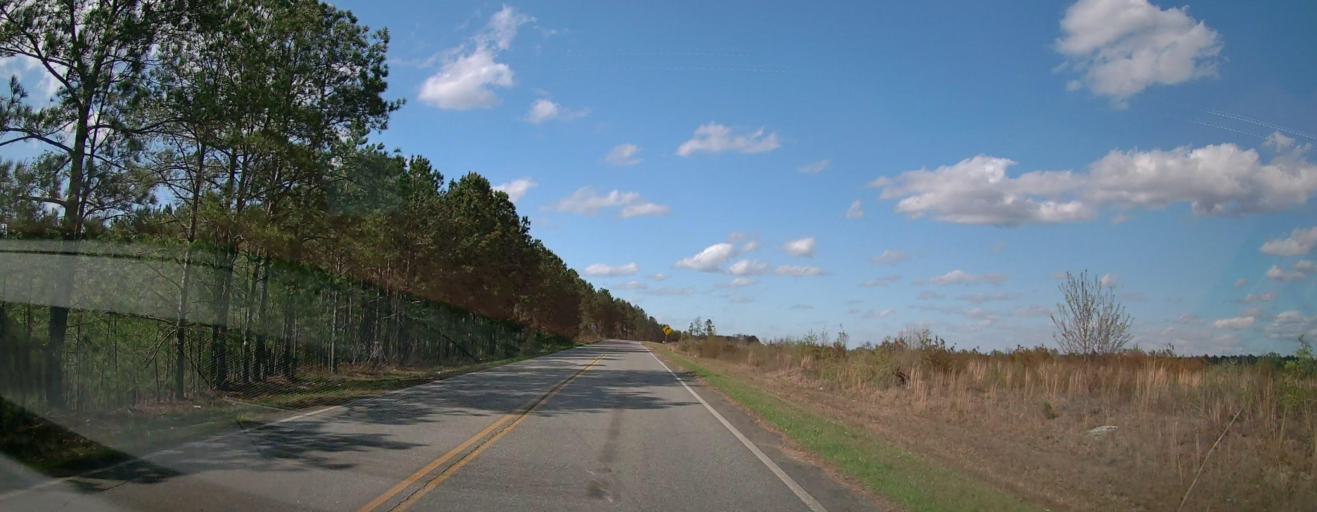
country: US
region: Georgia
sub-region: Wilkinson County
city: Gordon
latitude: 32.9455
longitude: -83.2900
